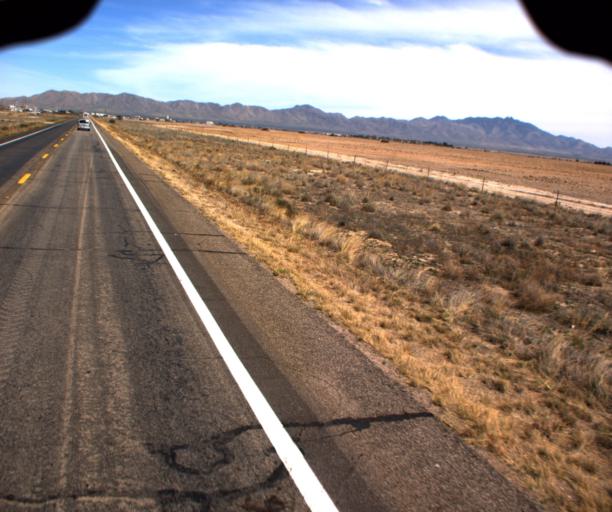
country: US
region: Arizona
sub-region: Cochise County
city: Willcox
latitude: 32.2334
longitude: -109.8541
